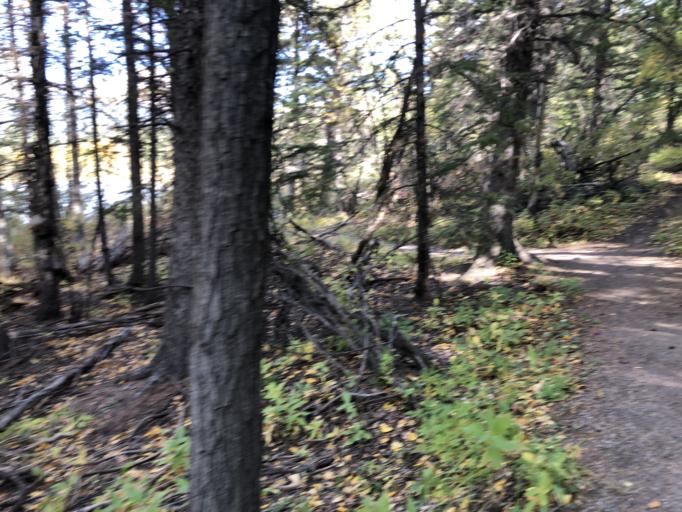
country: CA
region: Alberta
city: Canmore
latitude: 51.0713
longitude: -115.1146
